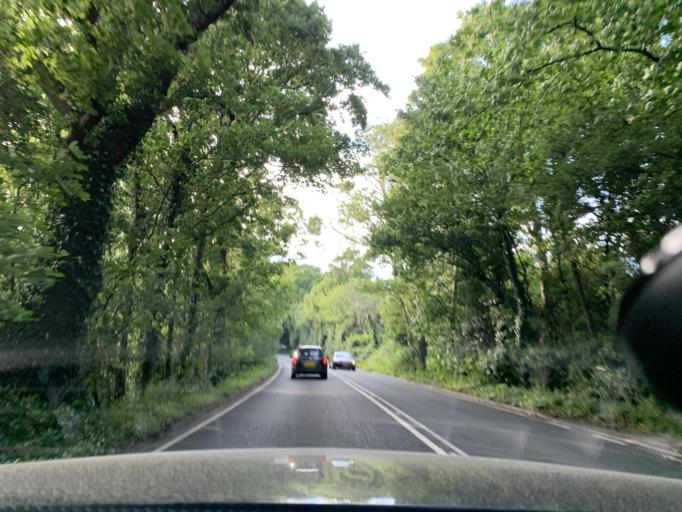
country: GB
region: England
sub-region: East Sussex
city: Battle
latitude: 50.9434
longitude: 0.5120
